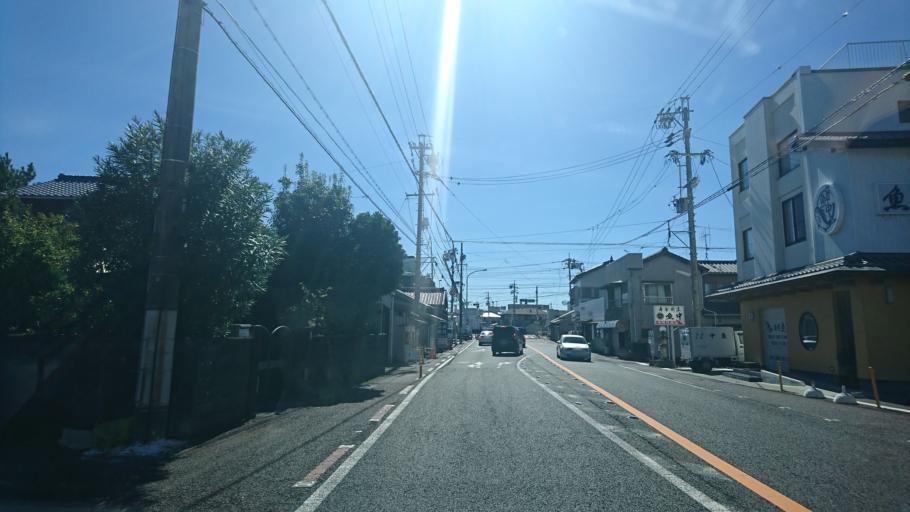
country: JP
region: Shizuoka
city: Shimada
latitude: 34.8388
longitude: 138.1794
